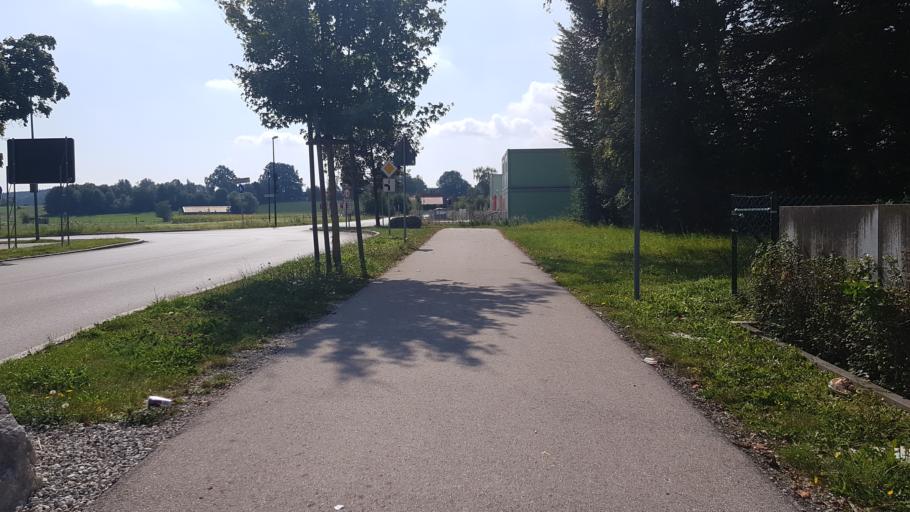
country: DE
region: Bavaria
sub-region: Upper Bavaria
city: Wessling
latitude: 48.0809
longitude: 11.2657
